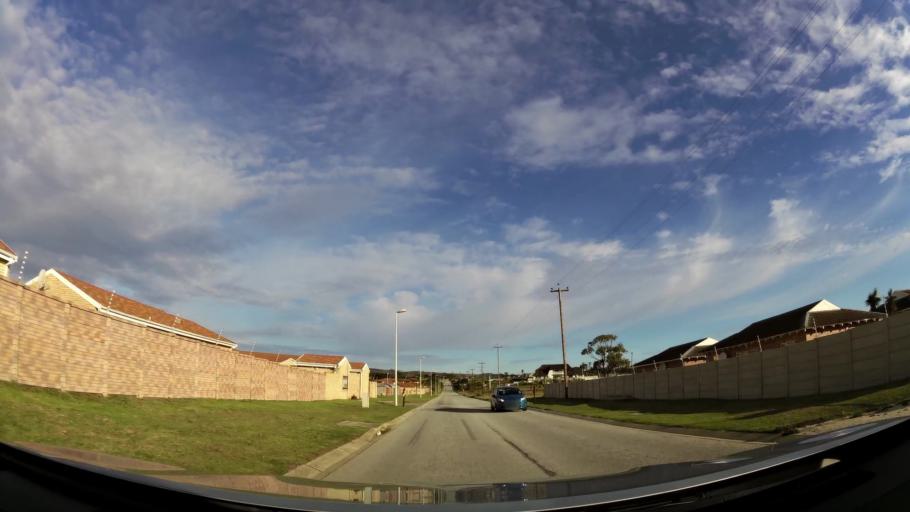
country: ZA
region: Eastern Cape
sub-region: Nelson Mandela Bay Metropolitan Municipality
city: Port Elizabeth
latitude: -33.9525
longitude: 25.4875
